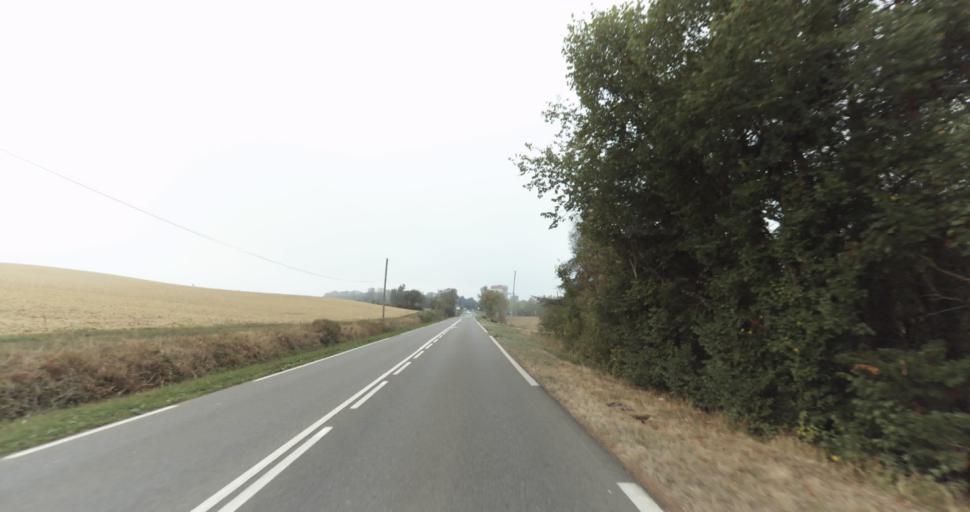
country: FR
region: Midi-Pyrenees
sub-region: Departement du Gers
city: Preignan
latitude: 43.6986
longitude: 0.6113
